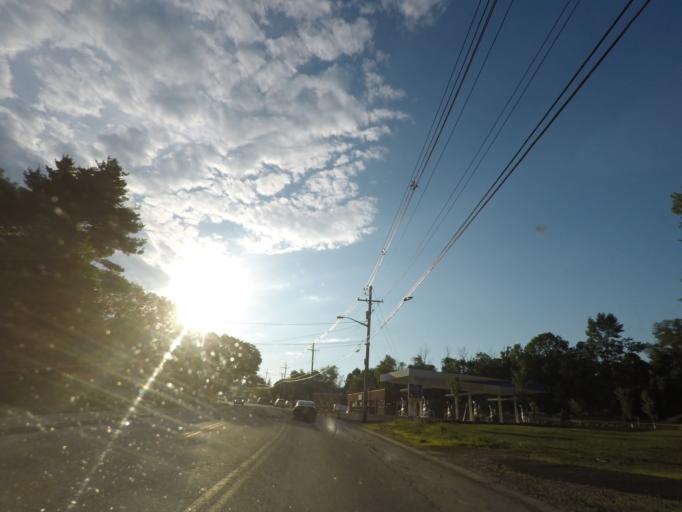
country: US
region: Massachusetts
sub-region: Worcester County
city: Southbridge
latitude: 42.0865
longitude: -72.0586
